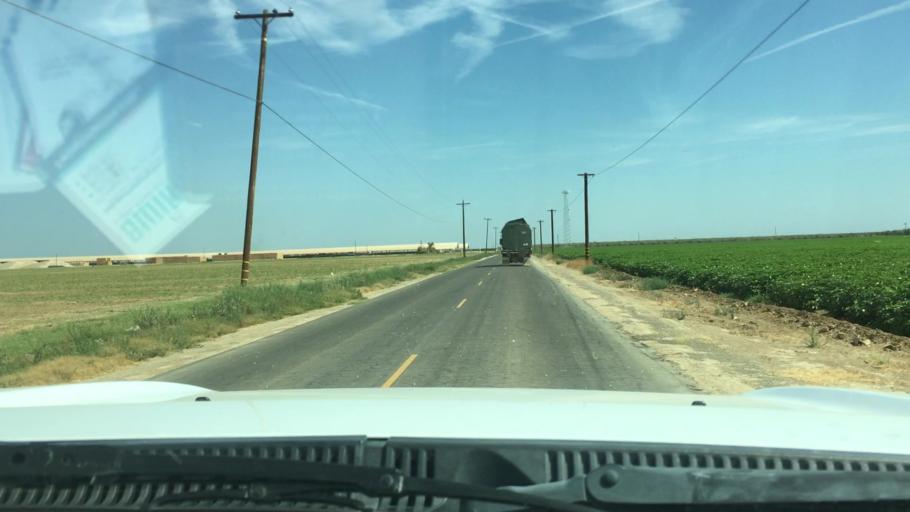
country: US
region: California
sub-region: Kern County
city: Shafter
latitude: 35.4649
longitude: -119.3681
